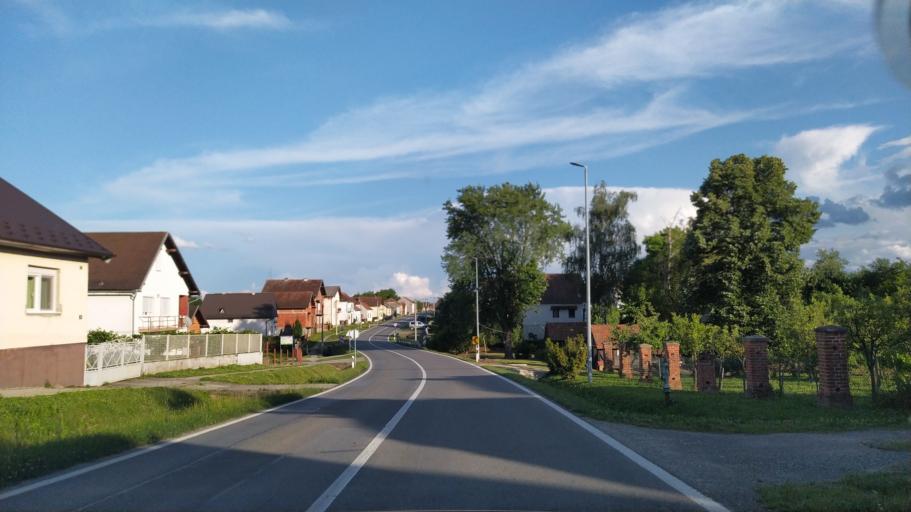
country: HR
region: Virovitick-Podravska
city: Slatina
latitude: 45.6614
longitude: 17.7716
